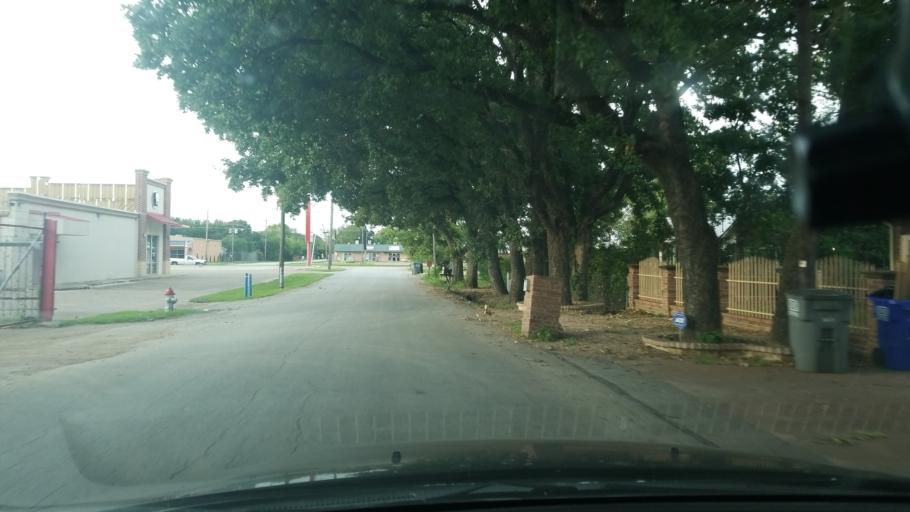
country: US
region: Texas
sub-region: Dallas County
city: Balch Springs
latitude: 32.7353
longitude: -96.6341
